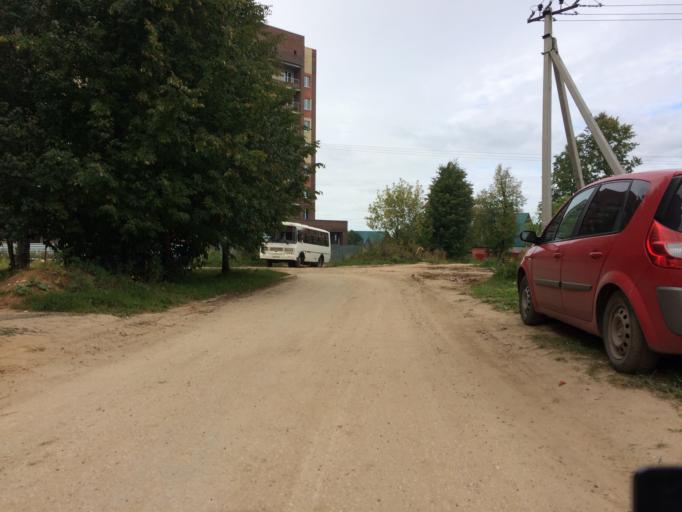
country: RU
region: Mariy-El
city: Yoshkar-Ola
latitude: 56.6532
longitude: 47.9701
